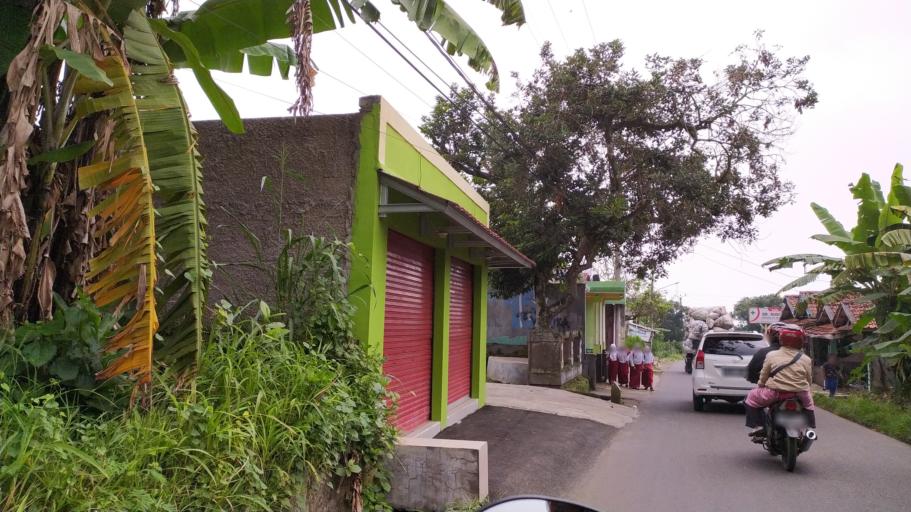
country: ID
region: West Java
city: Ciampea
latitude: -6.5971
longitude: 106.7043
